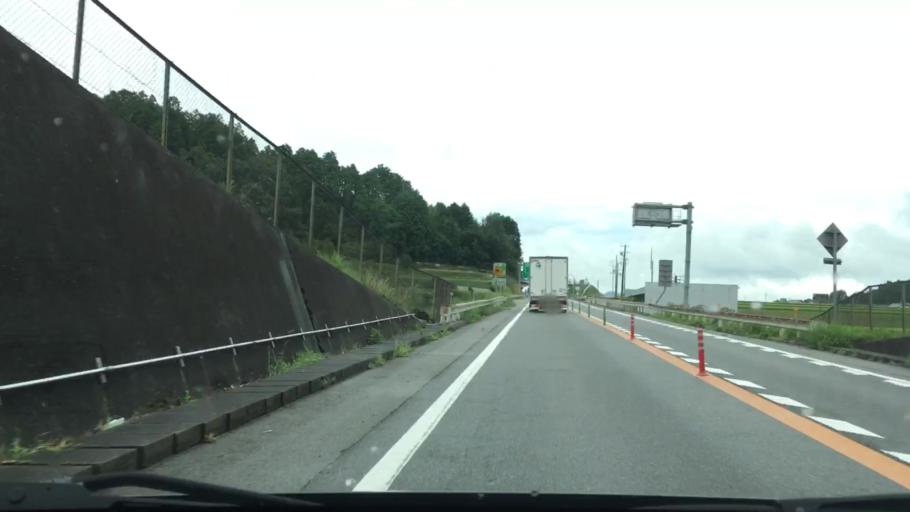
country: JP
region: Hyogo
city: Himeji
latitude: 34.9634
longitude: 134.7697
